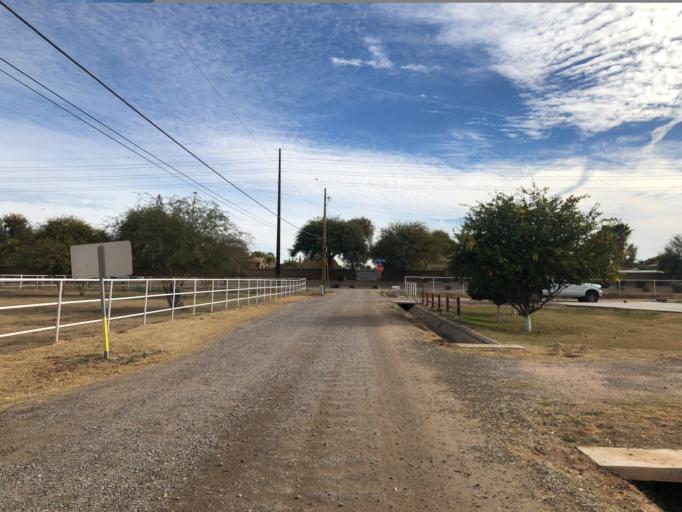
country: US
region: Arizona
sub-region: Maricopa County
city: Sun Lakes
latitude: 33.2281
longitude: -111.8074
